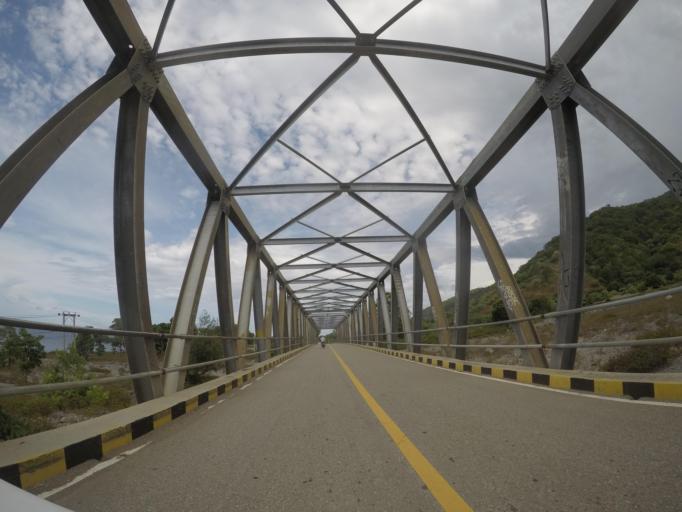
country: TL
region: Liquica
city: Maubara
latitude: -8.6221
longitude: 125.1701
